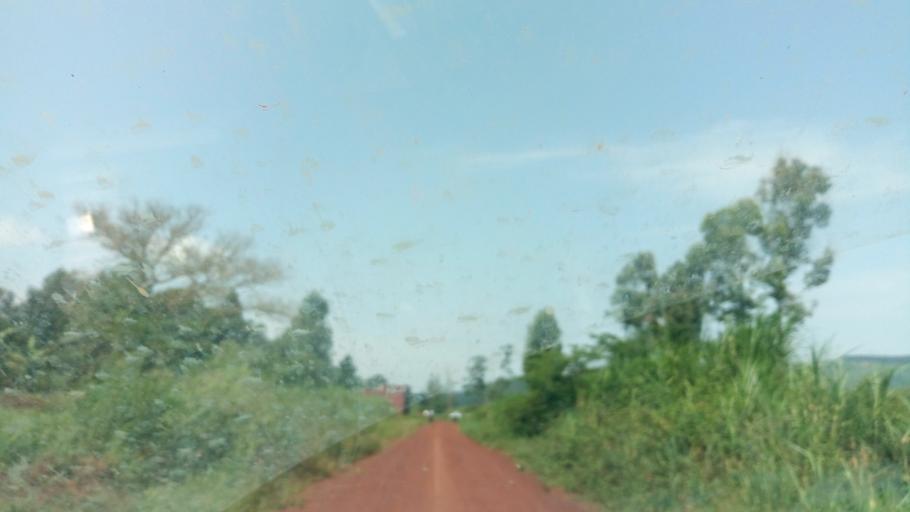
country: UG
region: Western Region
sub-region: Masindi District
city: Masindi
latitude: 1.6591
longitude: 31.8103
